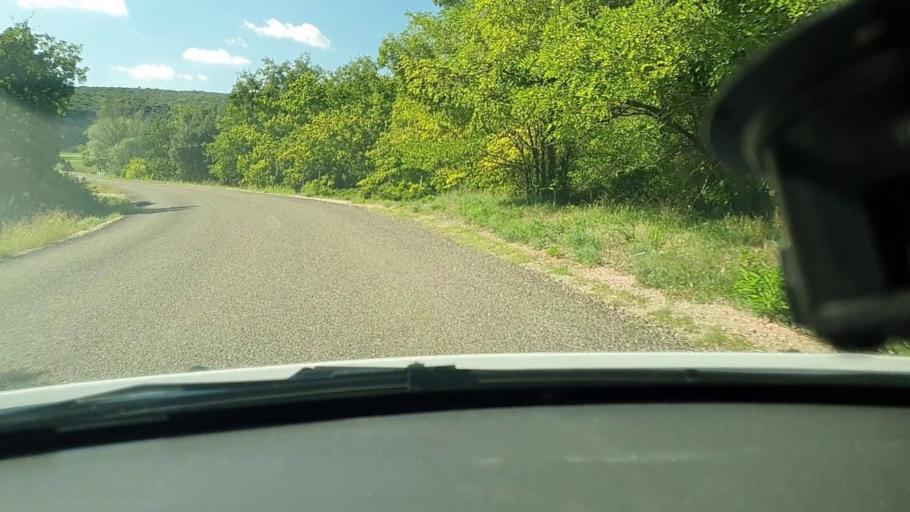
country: FR
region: Languedoc-Roussillon
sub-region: Departement du Gard
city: Goudargues
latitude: 44.1777
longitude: 4.4511
